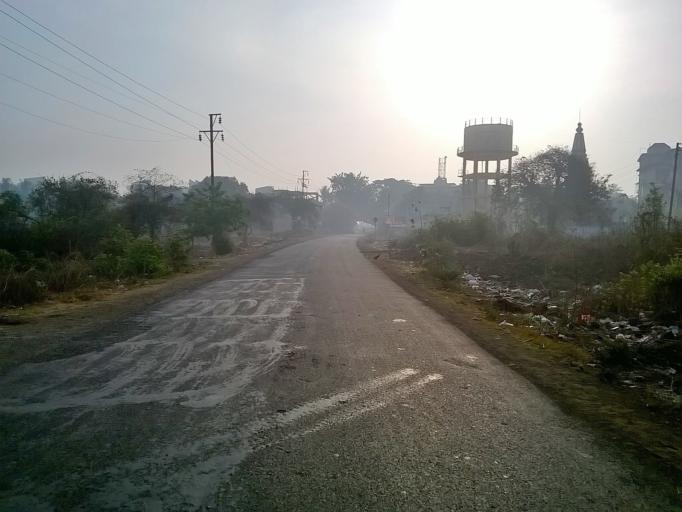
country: IN
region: Maharashtra
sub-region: Raigarh
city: Kalundri
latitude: 19.0112
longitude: 73.1572
